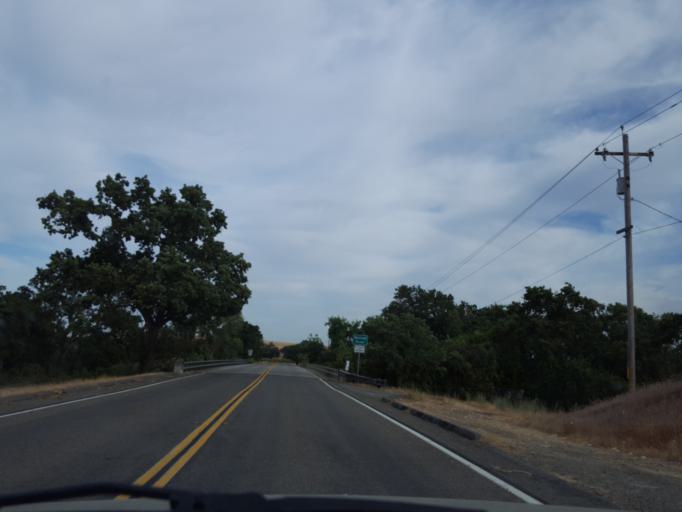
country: US
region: California
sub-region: Merced County
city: Winton
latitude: 37.5058
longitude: -120.4517
